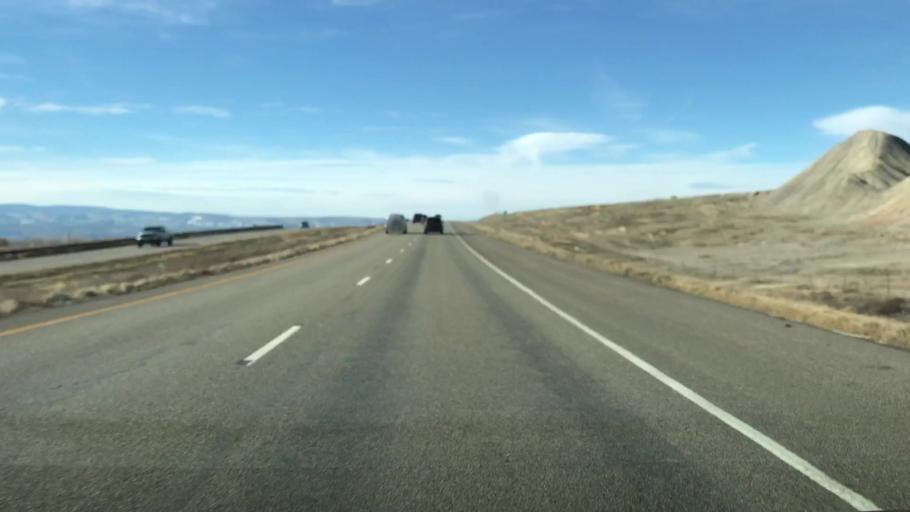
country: US
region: Colorado
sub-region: Mesa County
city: Clifton
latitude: 39.1140
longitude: -108.4050
